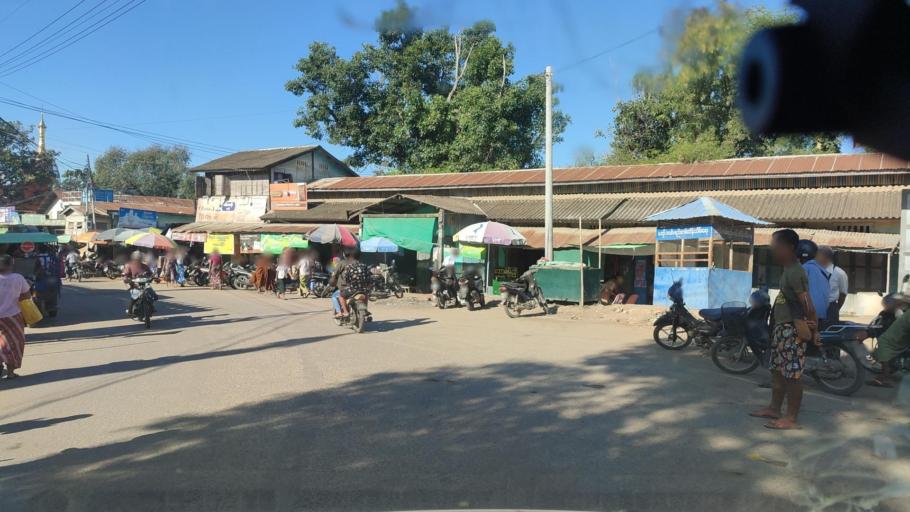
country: MM
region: Magway
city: Yenangyaung
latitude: 20.4632
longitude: 94.8715
